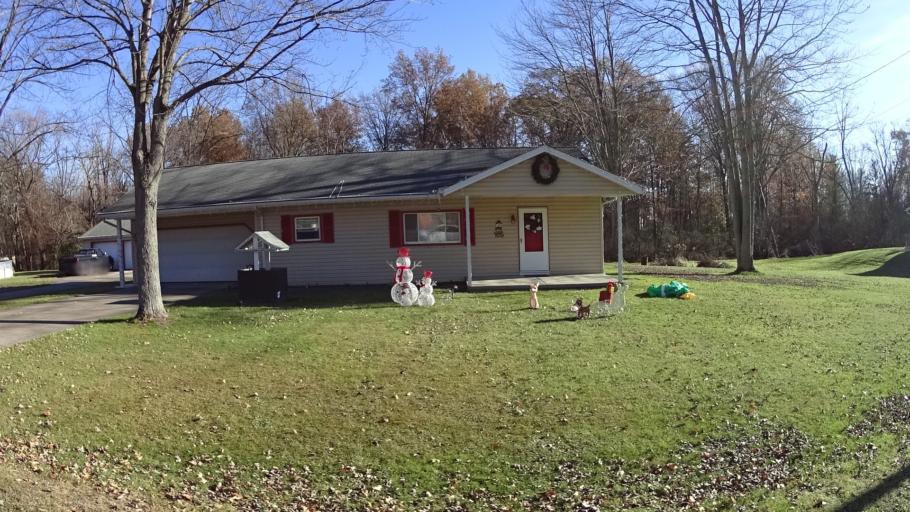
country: US
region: Ohio
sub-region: Lorain County
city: Elyria
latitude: 41.3285
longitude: -82.1360
